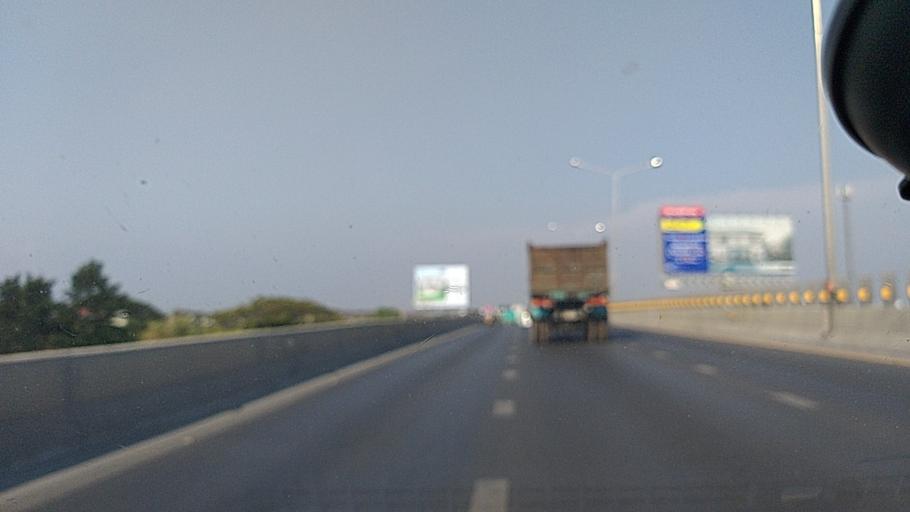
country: TH
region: Nonthaburi
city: Bang Bua Thong
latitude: 13.9274
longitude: 100.4389
